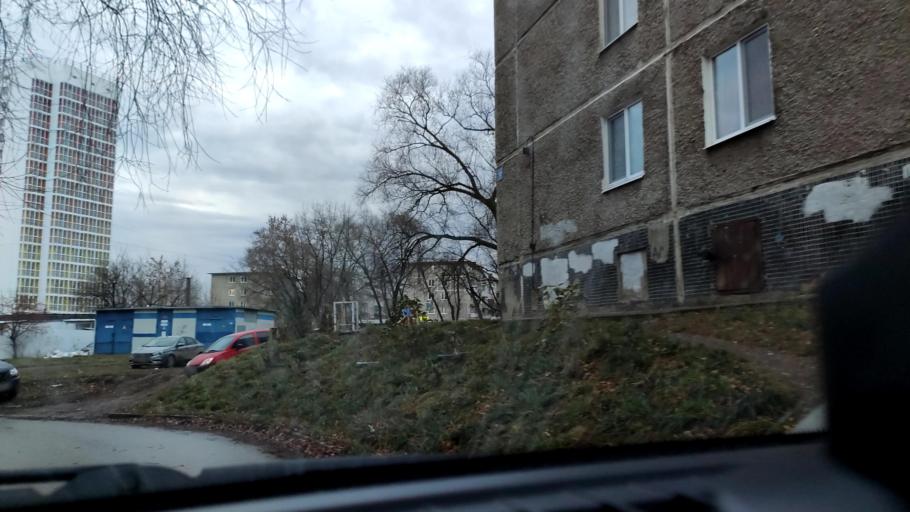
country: RU
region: Perm
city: Perm
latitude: 57.9786
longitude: 56.2755
